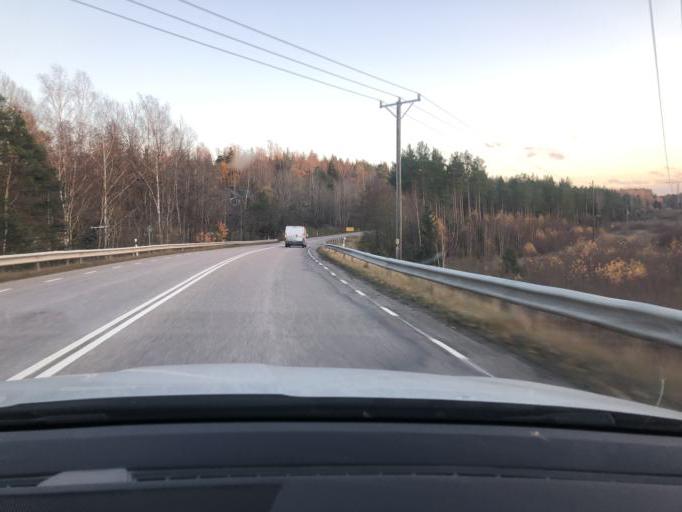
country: SE
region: Soedermanland
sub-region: Strangnas Kommun
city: Akers Styckebruk
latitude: 59.3081
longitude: 17.0902
